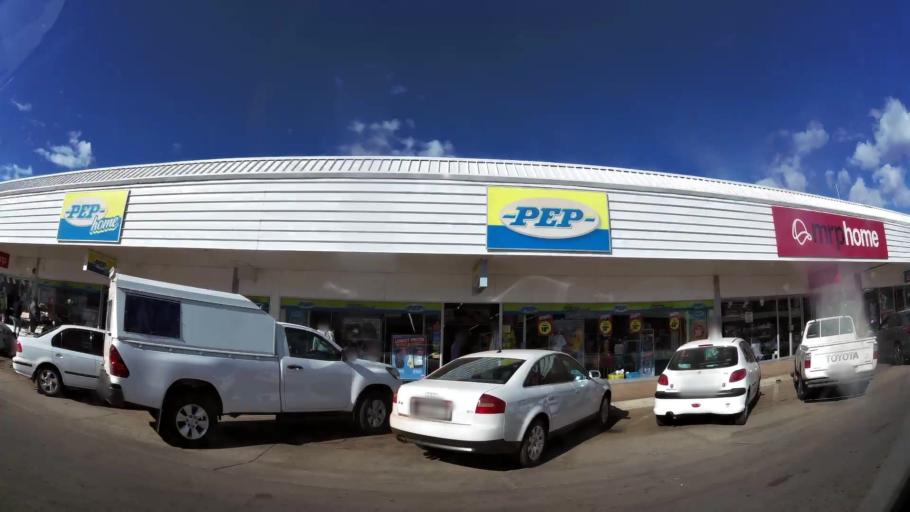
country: ZA
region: Limpopo
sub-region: Waterberg District Municipality
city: Bela-Bela
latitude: -24.8849
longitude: 28.2958
